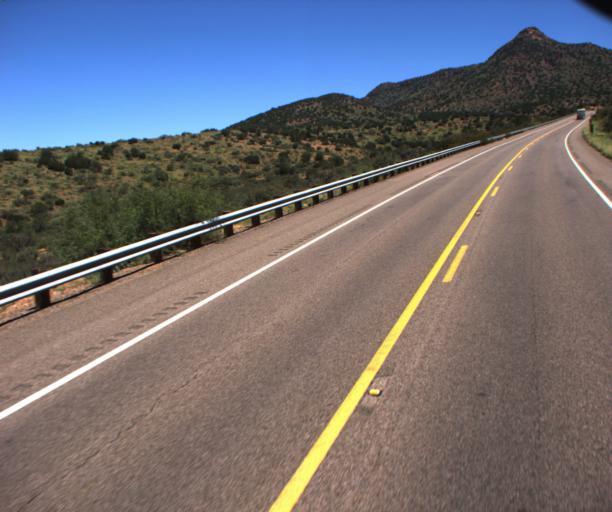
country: US
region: Arizona
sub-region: Gila County
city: Globe
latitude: 33.6057
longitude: -110.6306
